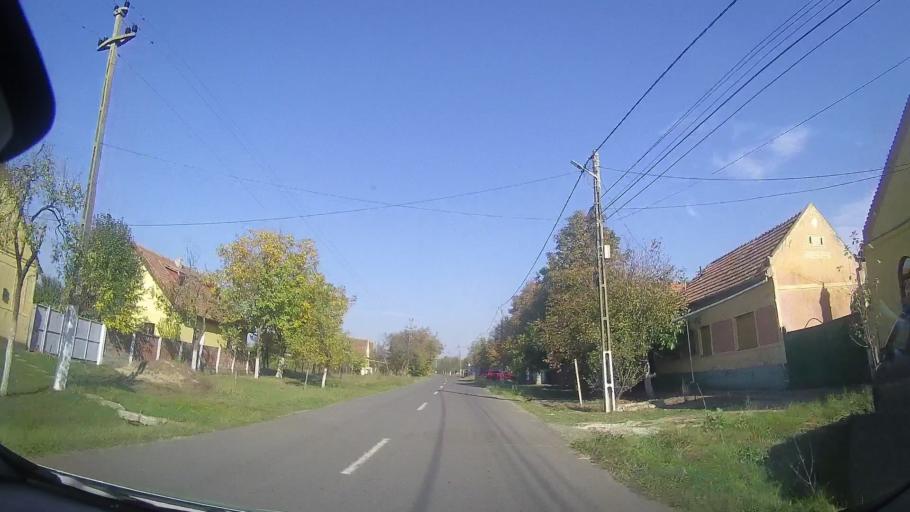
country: RO
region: Timis
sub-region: Comuna Topolovatu Mare
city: Topolovatu Mare
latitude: 45.8168
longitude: 21.5801
